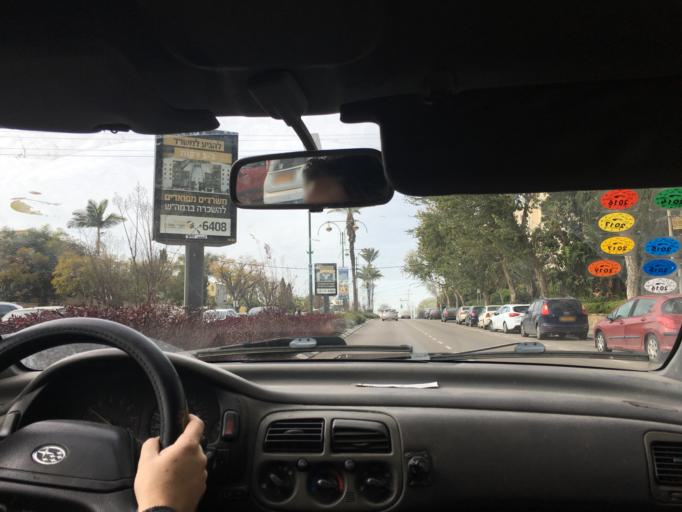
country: IL
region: Tel Aviv
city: Ramat HaSharon
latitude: 32.1373
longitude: 34.8405
